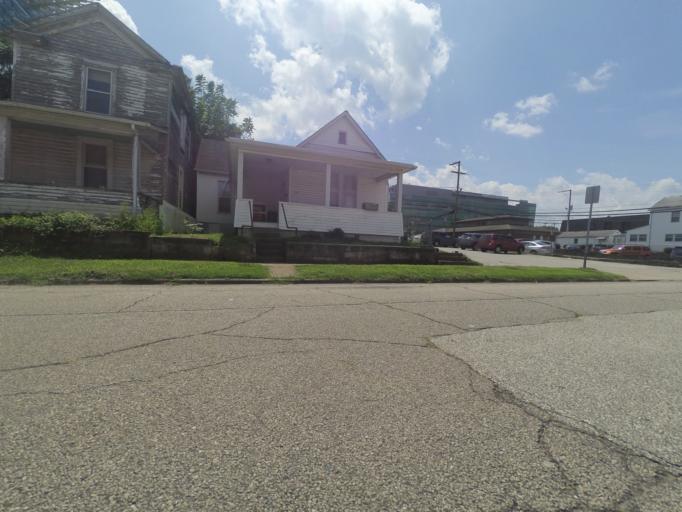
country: US
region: West Virginia
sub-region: Cabell County
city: Huntington
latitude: 38.4118
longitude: -82.4265
